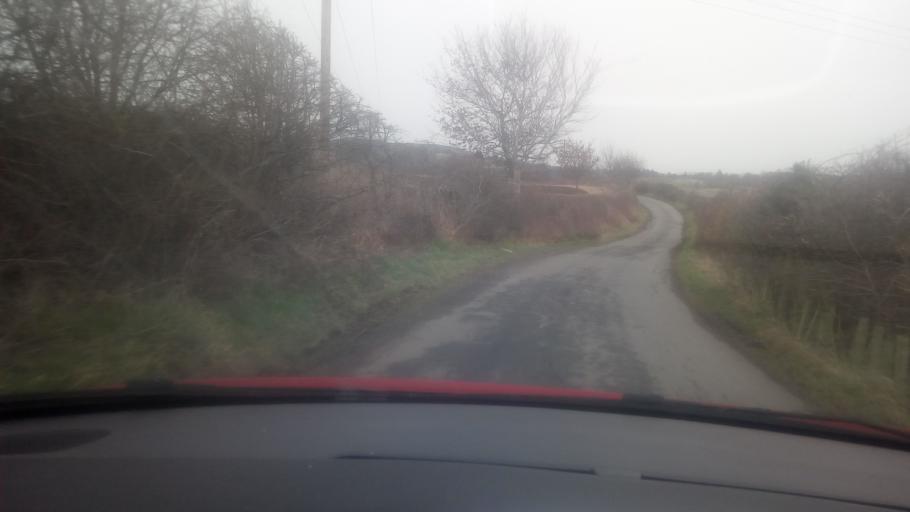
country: GB
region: Scotland
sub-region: The Scottish Borders
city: Jedburgh
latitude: 55.5032
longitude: -2.6025
